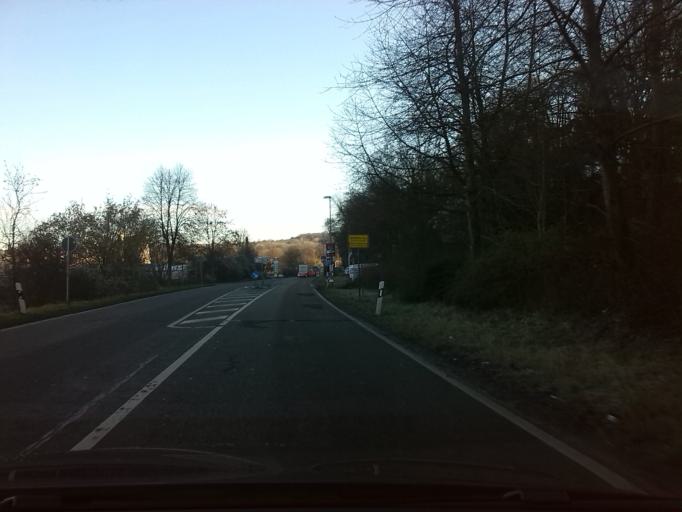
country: DE
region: Baden-Wuerttemberg
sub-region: Regierungsbezirk Stuttgart
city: Stuttgart Muehlhausen
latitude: 48.8700
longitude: 9.2696
